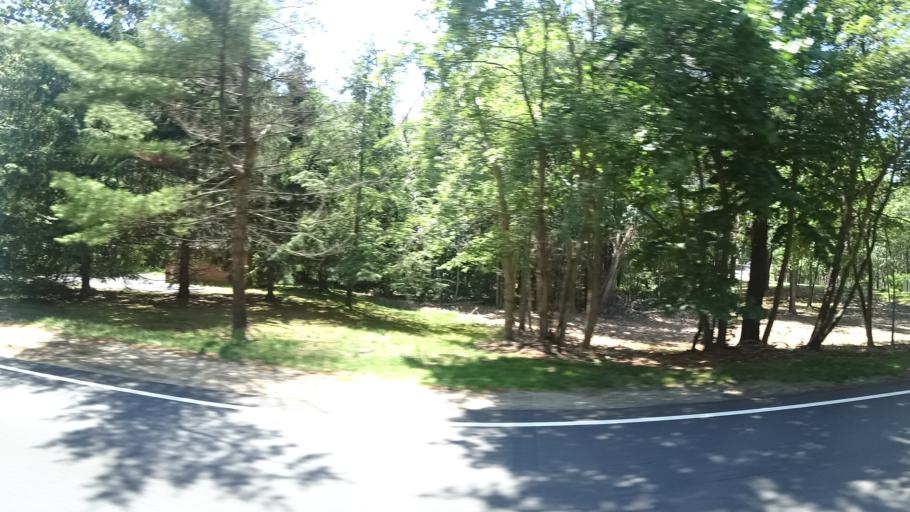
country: US
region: Massachusetts
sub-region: Norfolk County
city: Needham
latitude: 42.2505
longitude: -71.2235
